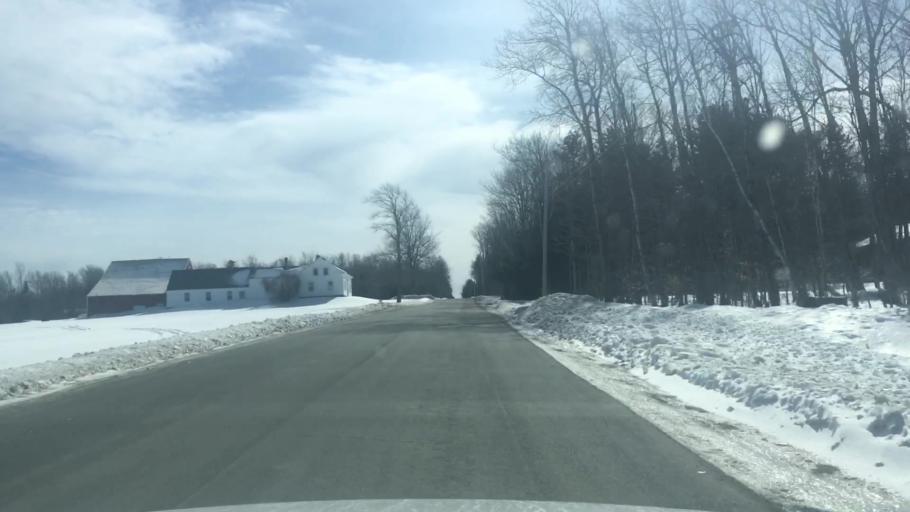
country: US
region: Maine
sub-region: Penobscot County
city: Holden
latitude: 44.7750
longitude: -68.6506
